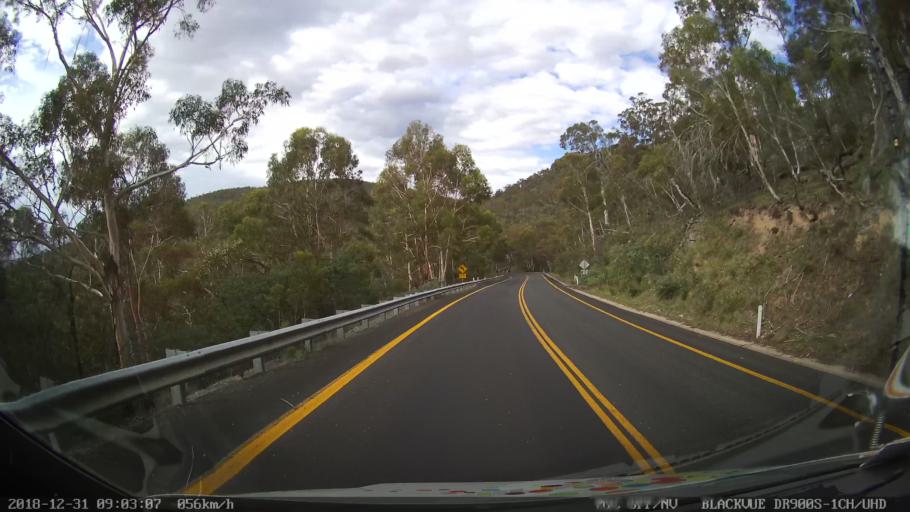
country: AU
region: New South Wales
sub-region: Snowy River
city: Jindabyne
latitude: -36.3454
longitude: 148.5812
